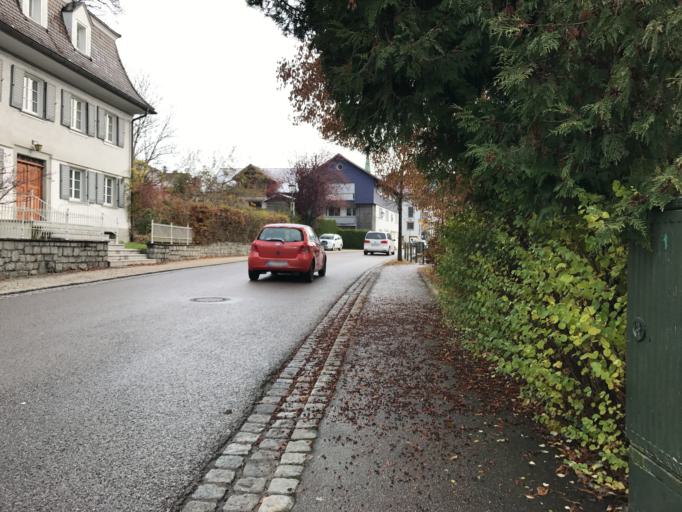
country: DE
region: Bavaria
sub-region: Swabia
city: Weiler-Simmerberg
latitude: 47.5822
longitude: 9.9123
